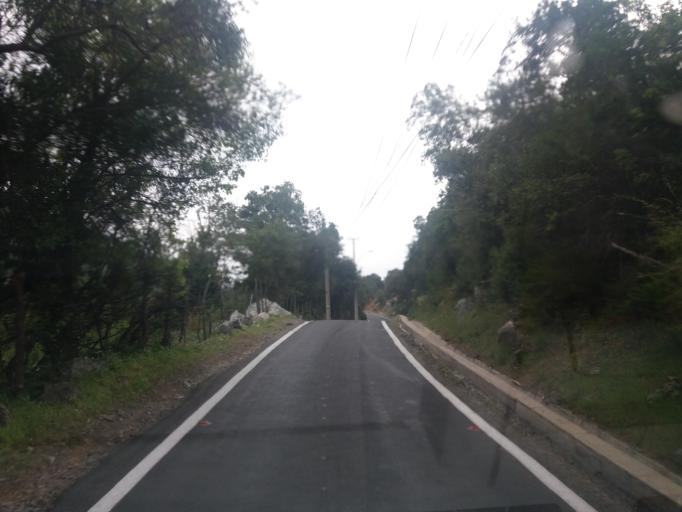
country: CL
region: Valparaiso
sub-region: Provincia de Marga Marga
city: Limache
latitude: -33.0381
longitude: -71.0931
